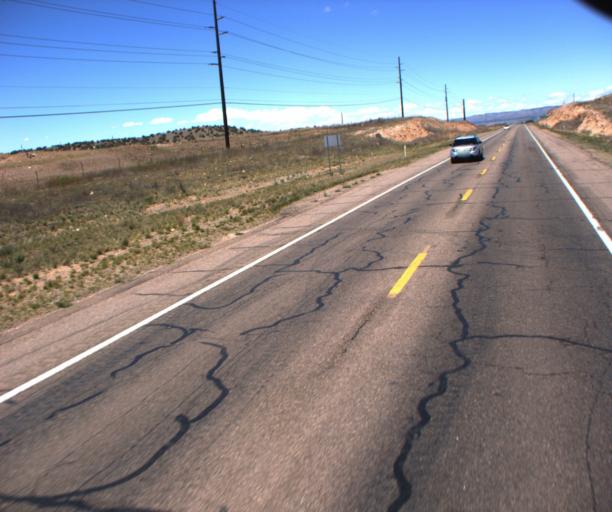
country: US
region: Arizona
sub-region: Yavapai County
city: Paulden
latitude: 34.8308
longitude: -112.4596
